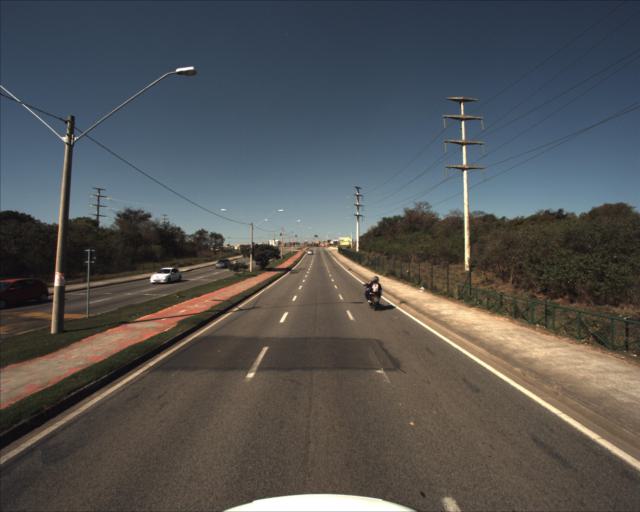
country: BR
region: Sao Paulo
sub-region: Sorocaba
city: Sorocaba
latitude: -23.4529
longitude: -47.4596
